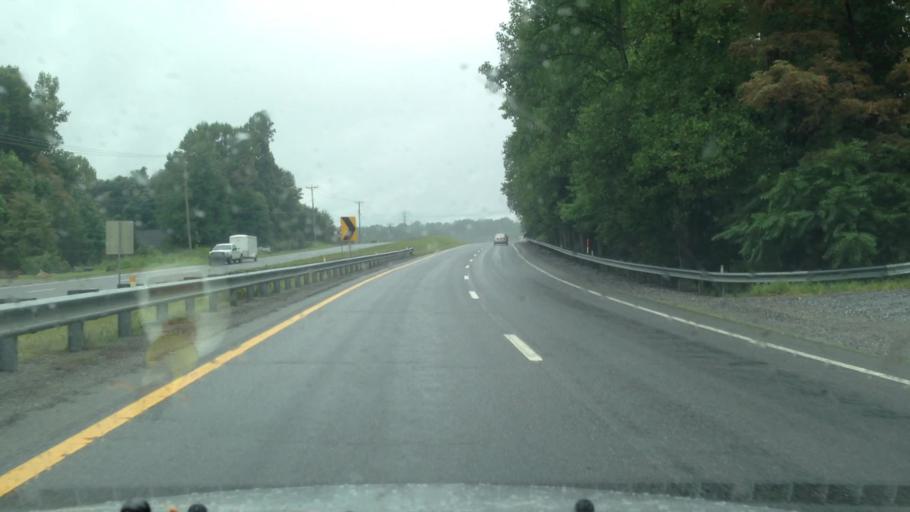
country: US
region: Virginia
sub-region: Henry County
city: Stanleytown
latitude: 36.8212
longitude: -79.9286
